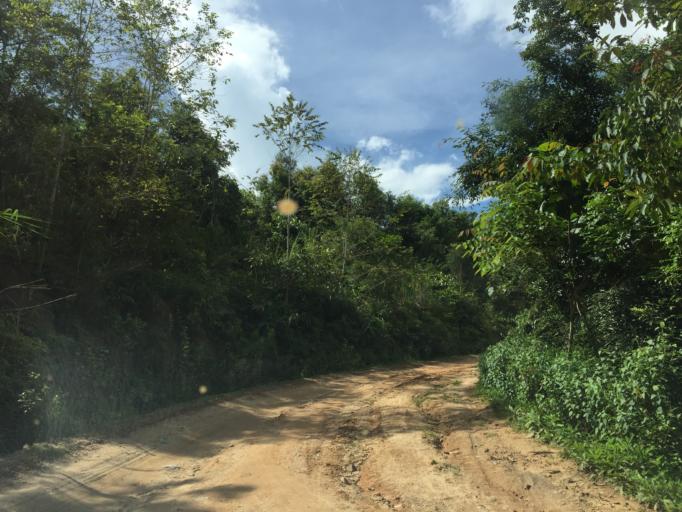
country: LA
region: Xiangkhoang
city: Muang Phonsavan
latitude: 19.3395
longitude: 103.5123
